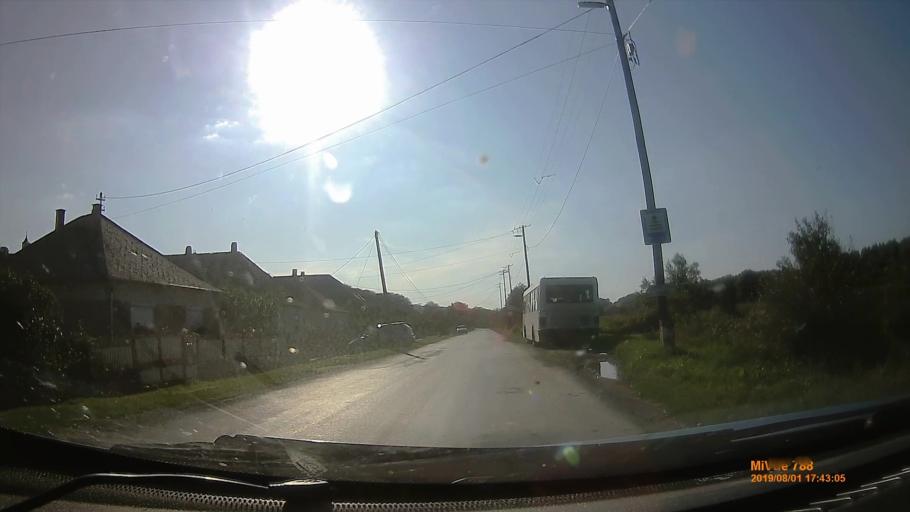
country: HU
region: Baranya
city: Sasd
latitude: 46.1916
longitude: 18.1537
